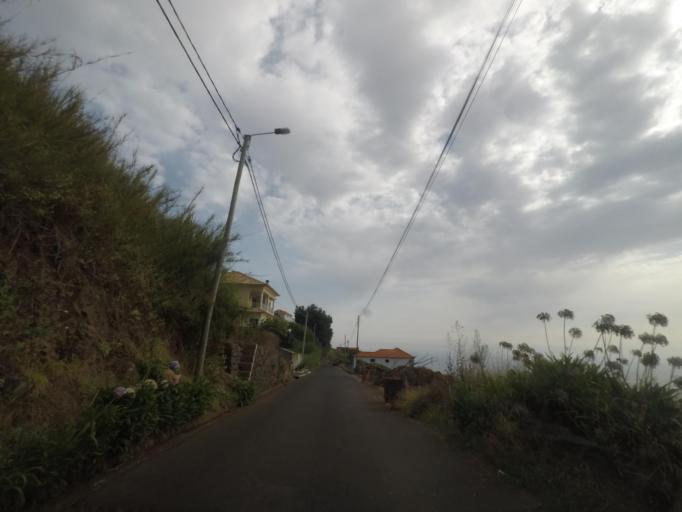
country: PT
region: Madeira
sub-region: Calheta
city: Arco da Calheta
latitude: 32.7347
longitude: -17.1541
